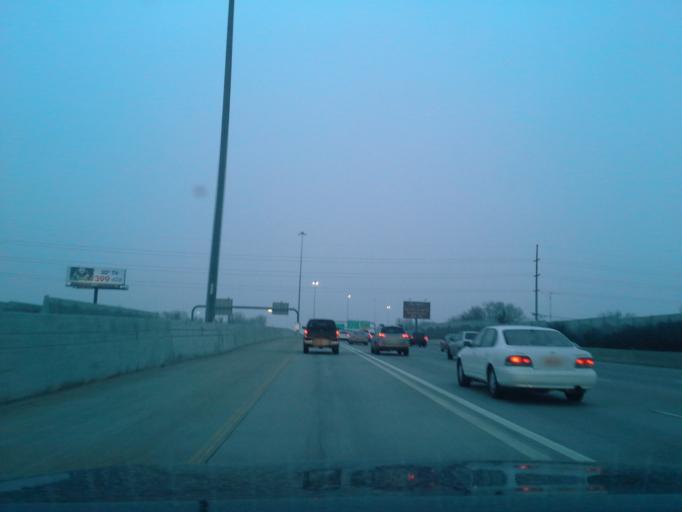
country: US
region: Utah
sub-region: Salt Lake County
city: Murray
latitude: 40.6440
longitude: -111.9029
